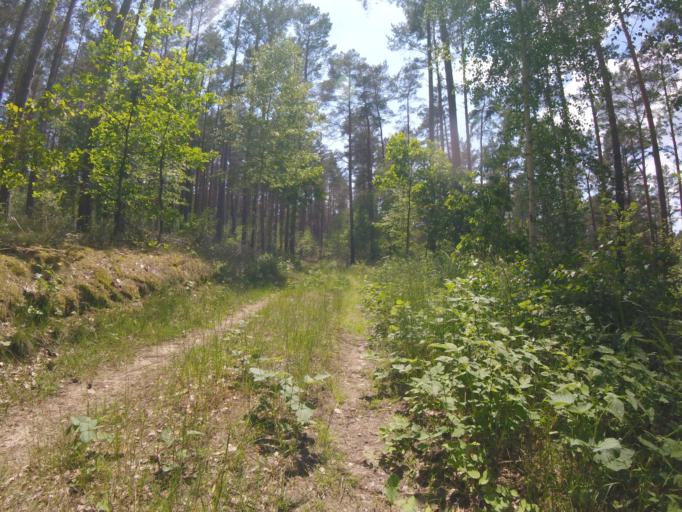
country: DE
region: Brandenburg
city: Teupitz
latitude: 52.1049
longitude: 13.5953
